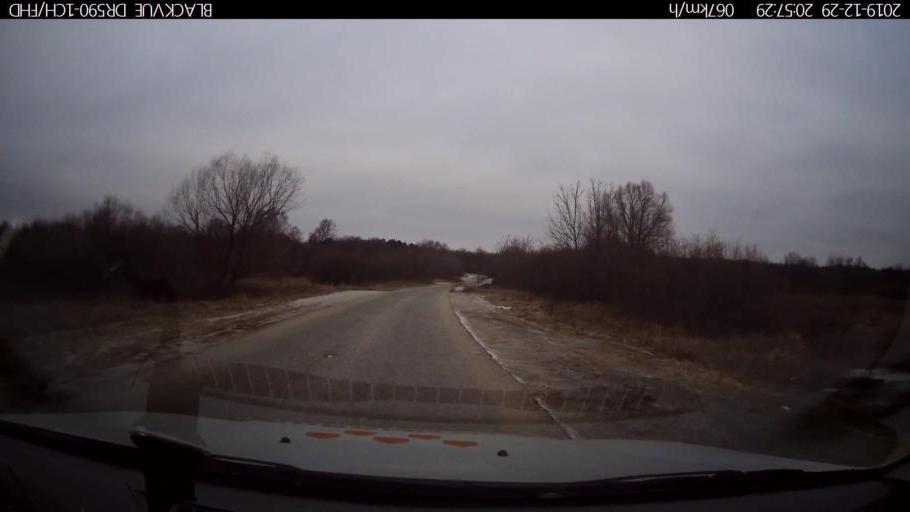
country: RU
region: Nizjnij Novgorod
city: Afonino
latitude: 56.1614
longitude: 43.9909
